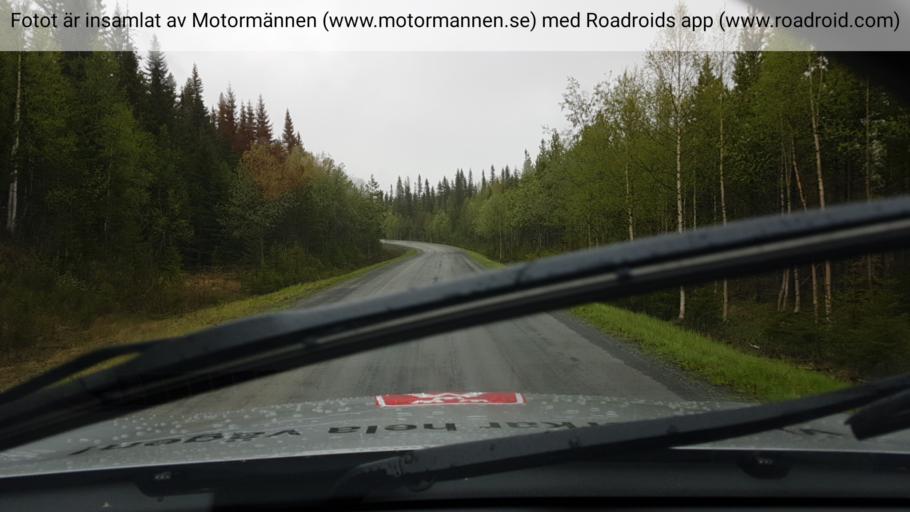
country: SE
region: Jaemtland
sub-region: Krokoms Kommun
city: Valla
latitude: 63.0952
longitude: 13.8950
